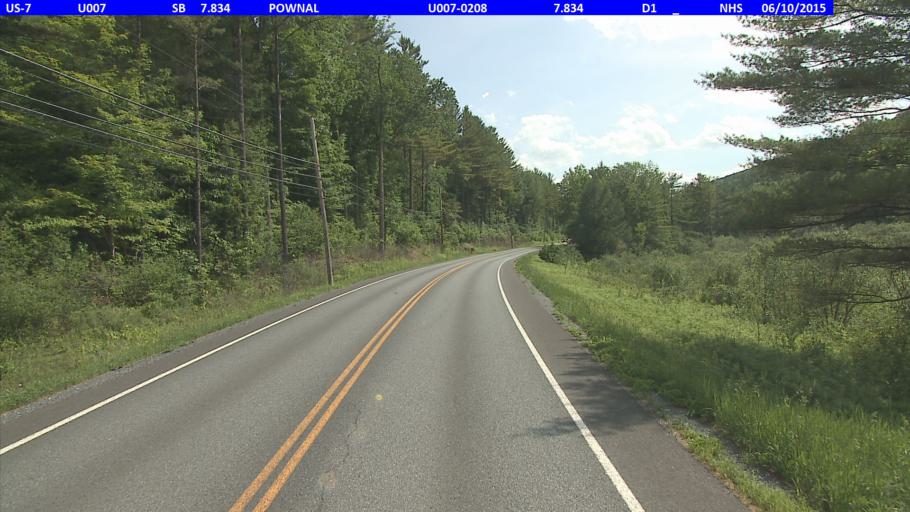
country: US
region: Vermont
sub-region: Bennington County
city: Bennington
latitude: 42.8355
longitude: -73.1993
